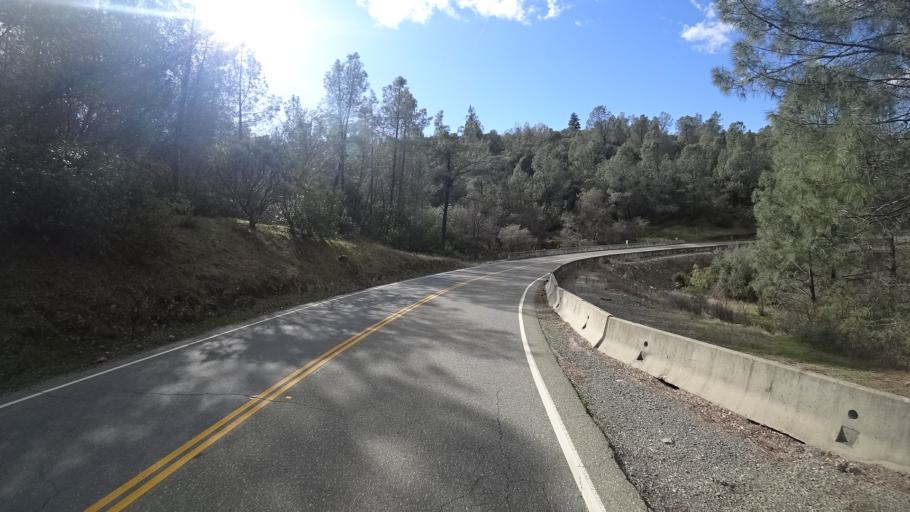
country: US
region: California
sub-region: Butte County
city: Oroville East
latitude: 39.5296
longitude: -121.4948
